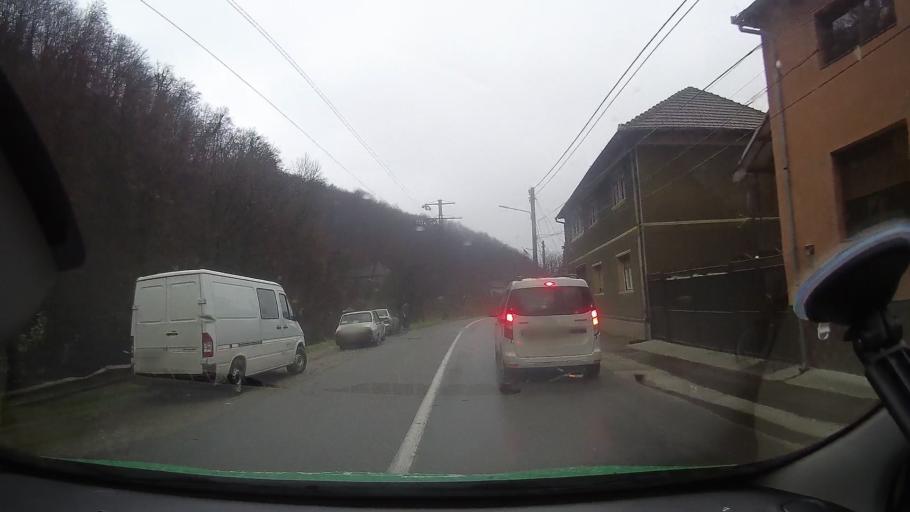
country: RO
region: Arad
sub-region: Comuna Moneasa
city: Moneasa
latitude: 46.4505
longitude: 22.2475
